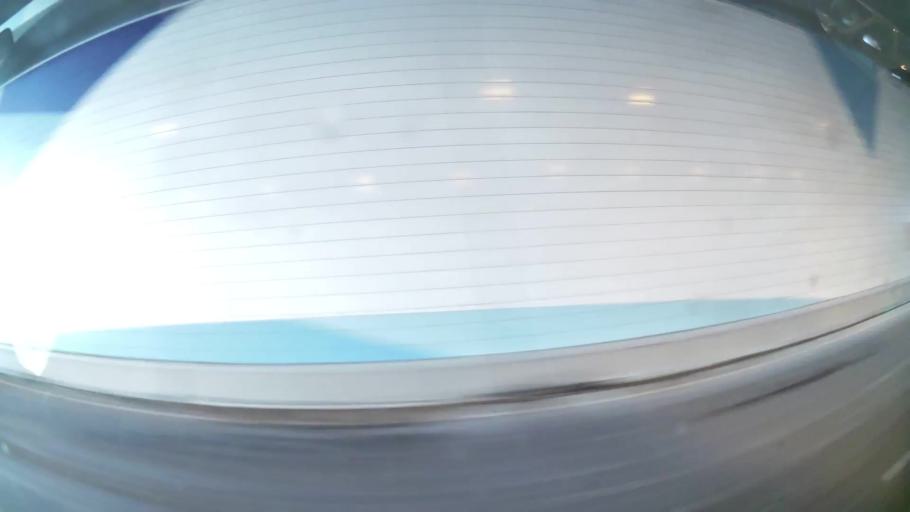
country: AE
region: Abu Dhabi
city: Abu Dhabi
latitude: 24.4721
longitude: 54.3922
